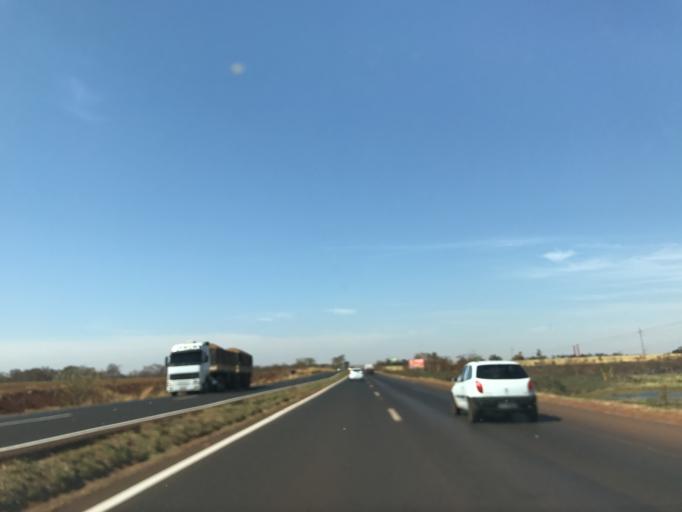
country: BR
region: Goias
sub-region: Itumbiara
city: Itumbiara
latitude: -18.4710
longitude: -49.1884
